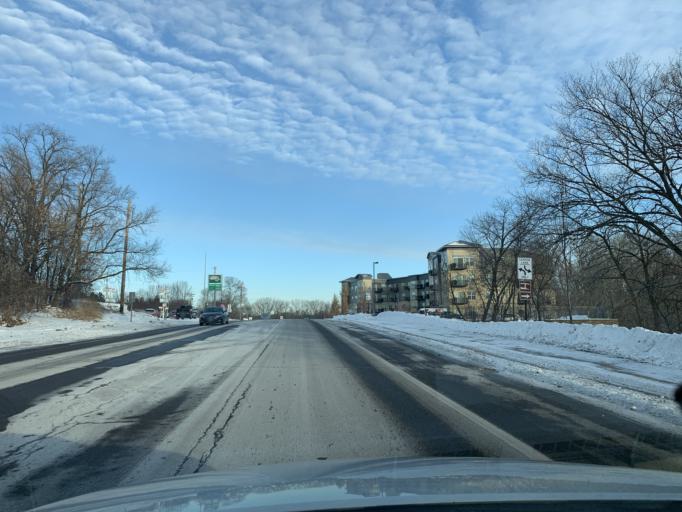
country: US
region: Minnesota
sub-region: Hennepin County
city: Minnetonka Mills
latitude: 44.9451
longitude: -93.4044
